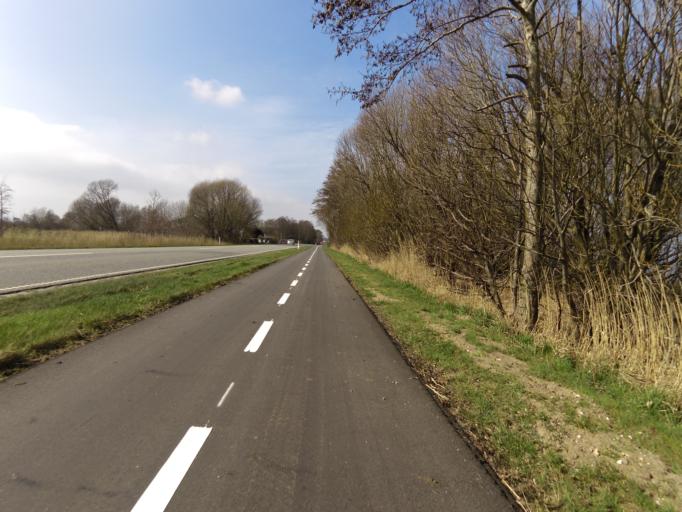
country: DK
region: Central Jutland
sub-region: Struer Kommune
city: Struer
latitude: 56.4700
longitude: 8.6336
